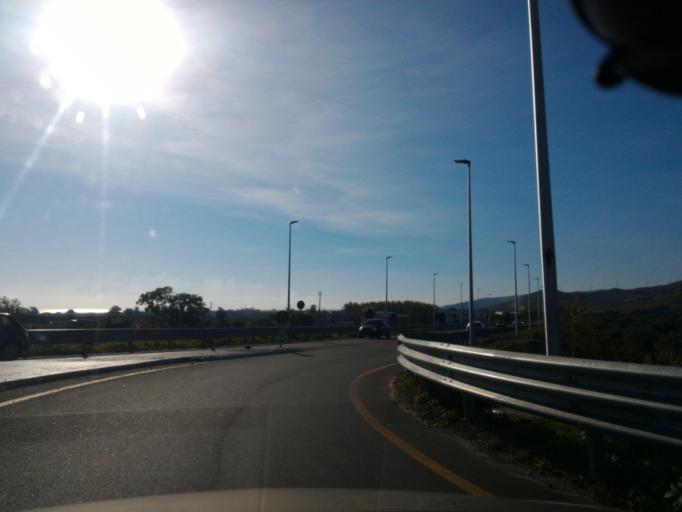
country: IT
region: Calabria
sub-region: Provincia di Crotone
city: Ciro Marina
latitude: 39.3591
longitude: 17.1113
